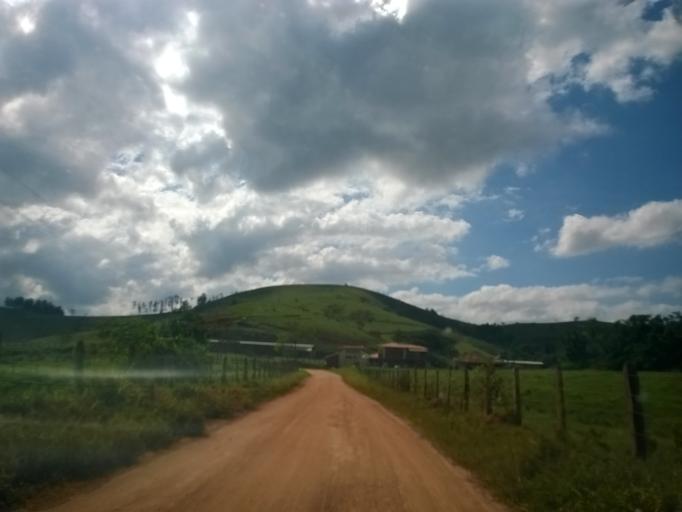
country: BR
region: Minas Gerais
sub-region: Visconde Do Rio Branco
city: Visconde do Rio Branco
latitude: -21.0478
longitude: -42.8992
